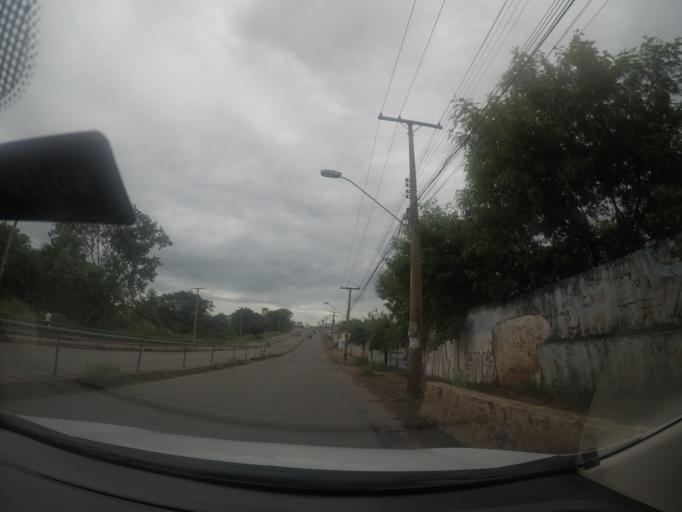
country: BR
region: Goias
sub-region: Goiania
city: Goiania
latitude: -16.6654
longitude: -49.3158
